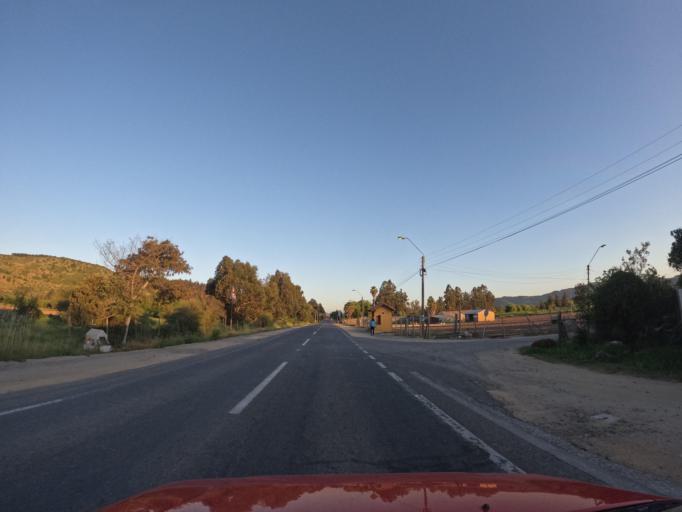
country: CL
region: Maule
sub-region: Provincia de Talca
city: Talca
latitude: -35.0839
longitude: -71.6701
